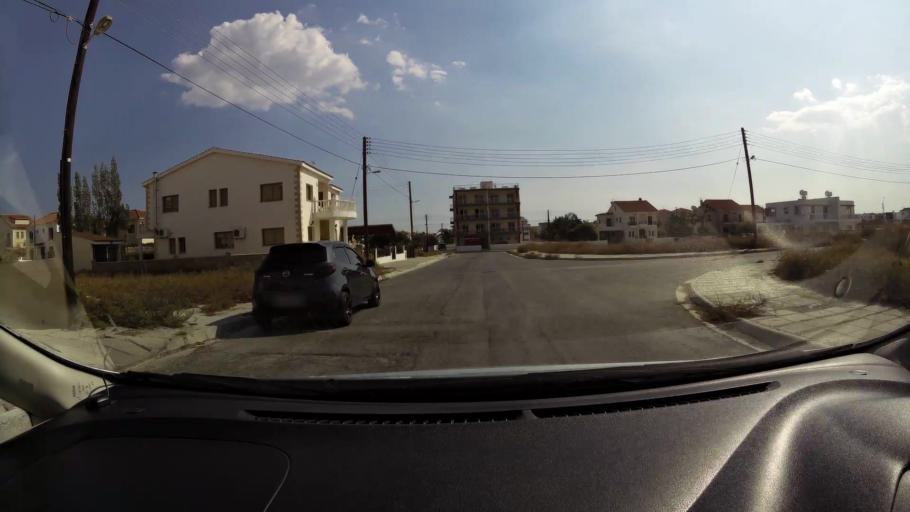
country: CY
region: Larnaka
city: Dhromolaxia
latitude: 34.9064
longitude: 33.5840
